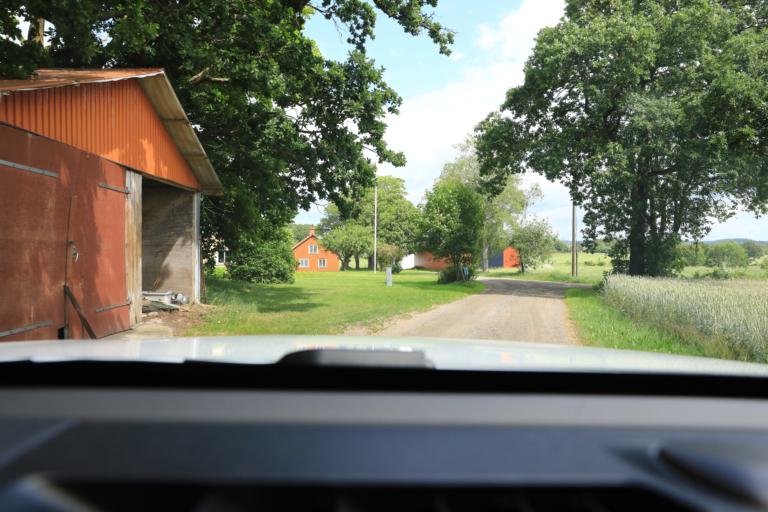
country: SE
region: Halland
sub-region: Varbergs Kommun
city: Tvaaker
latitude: 57.1062
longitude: 12.4023
